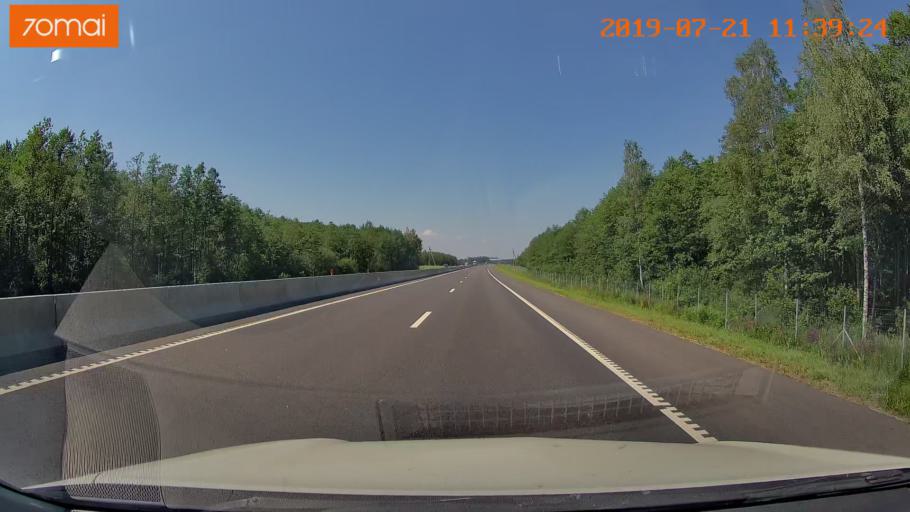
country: BY
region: Grodnenskaya
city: Lyubcha
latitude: 53.9602
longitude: 26.2003
